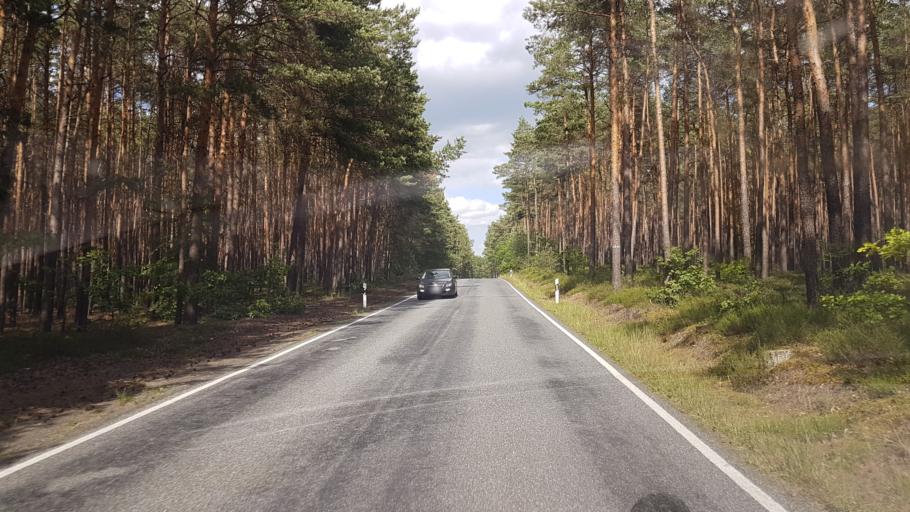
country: DE
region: Brandenburg
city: Guteborn
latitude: 51.4144
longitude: 13.9233
